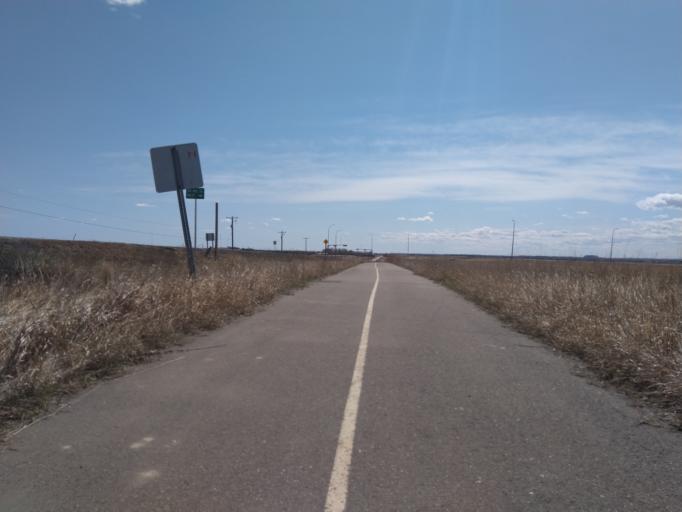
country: CA
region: Alberta
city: Chestermere
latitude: 50.9498
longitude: -113.9122
